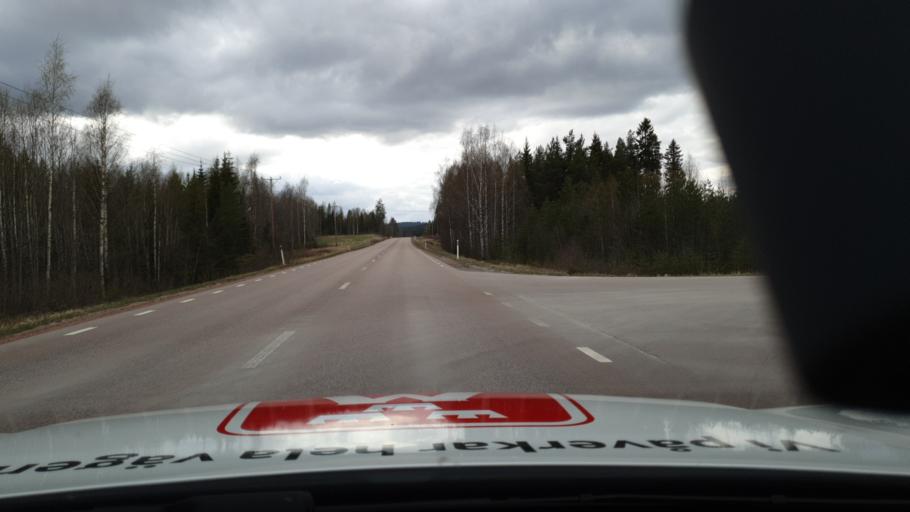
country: SE
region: Jaemtland
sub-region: Braecke Kommun
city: Braecke
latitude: 63.1627
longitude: 15.7054
